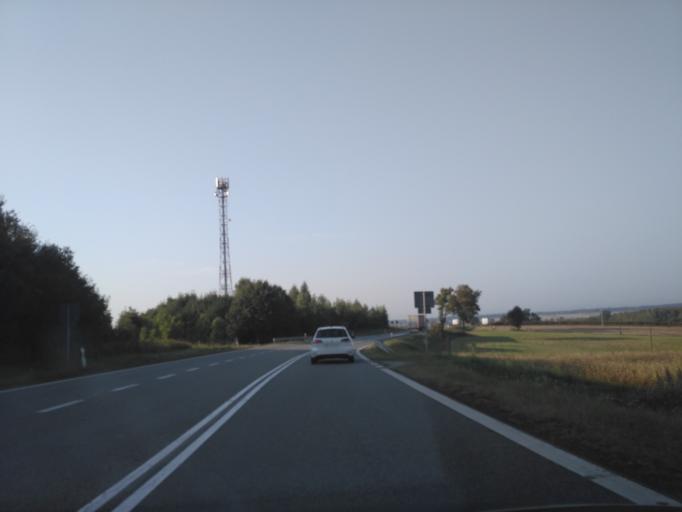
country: PL
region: Lublin Voivodeship
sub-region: Powiat janowski
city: Modliborzyce
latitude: 50.7688
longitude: 22.3252
